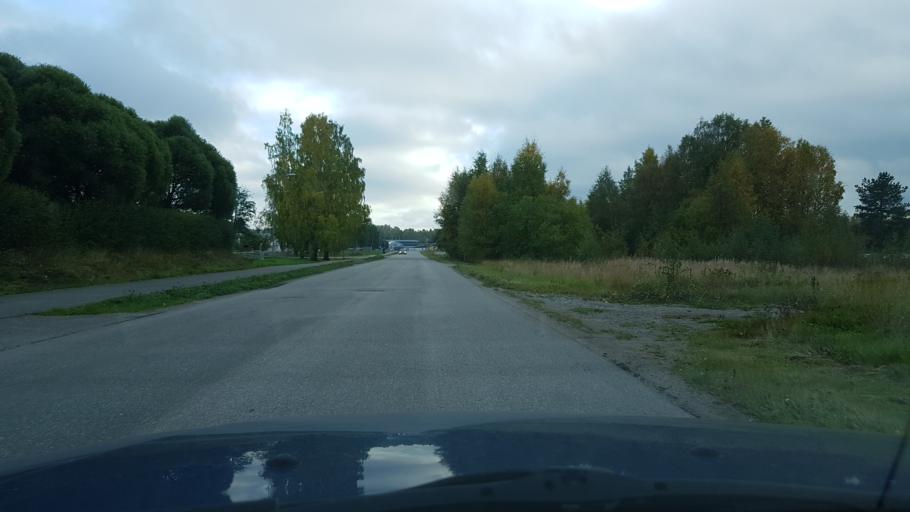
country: SE
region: Norrbotten
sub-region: Pitea Kommun
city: Bergsviken
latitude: 65.3440
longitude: 21.4090
